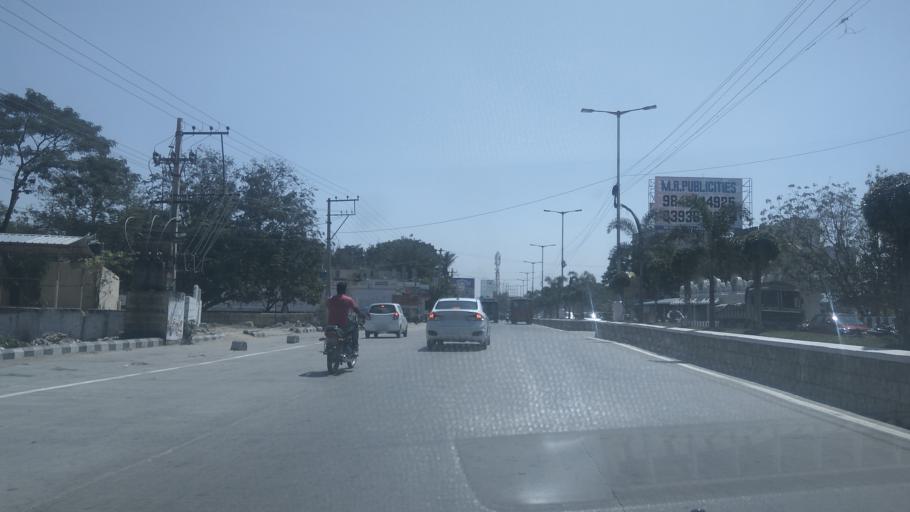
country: IN
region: Andhra Pradesh
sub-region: Chittoor
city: Tirupati
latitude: 13.6102
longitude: 79.4454
